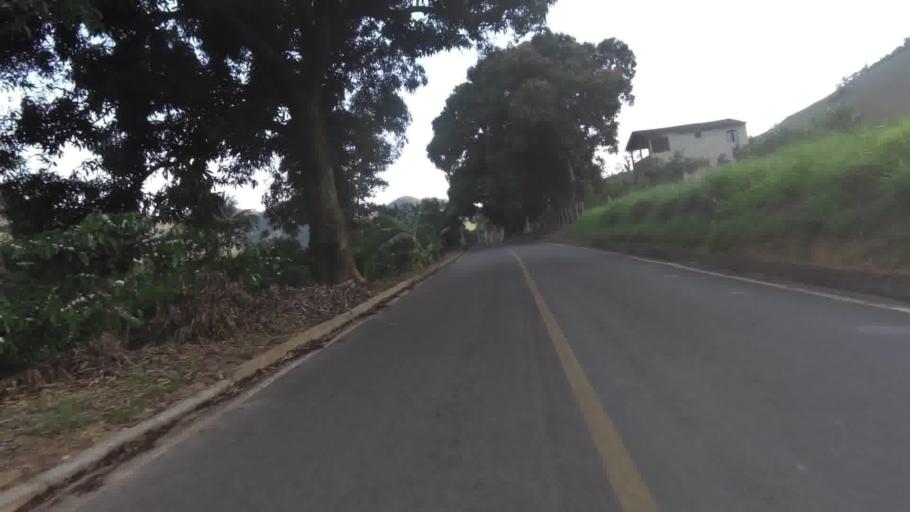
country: BR
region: Espirito Santo
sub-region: Alfredo Chaves
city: Alfredo Chaves
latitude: -20.5927
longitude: -40.7069
